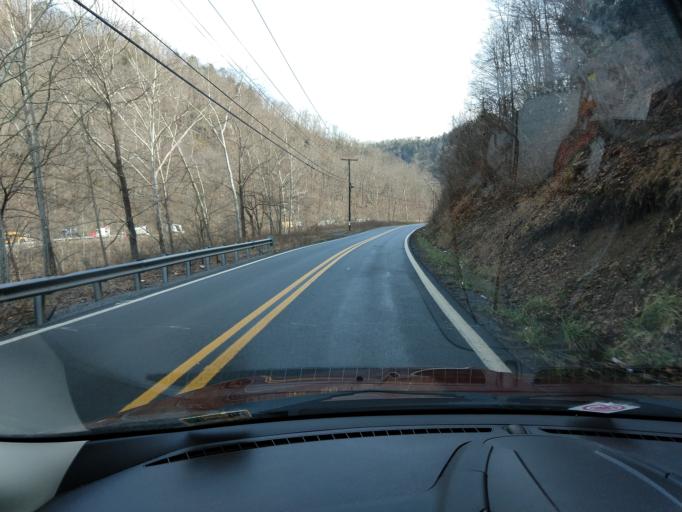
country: US
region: West Virginia
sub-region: McDowell County
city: Welch
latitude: 37.3398
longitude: -81.7378
